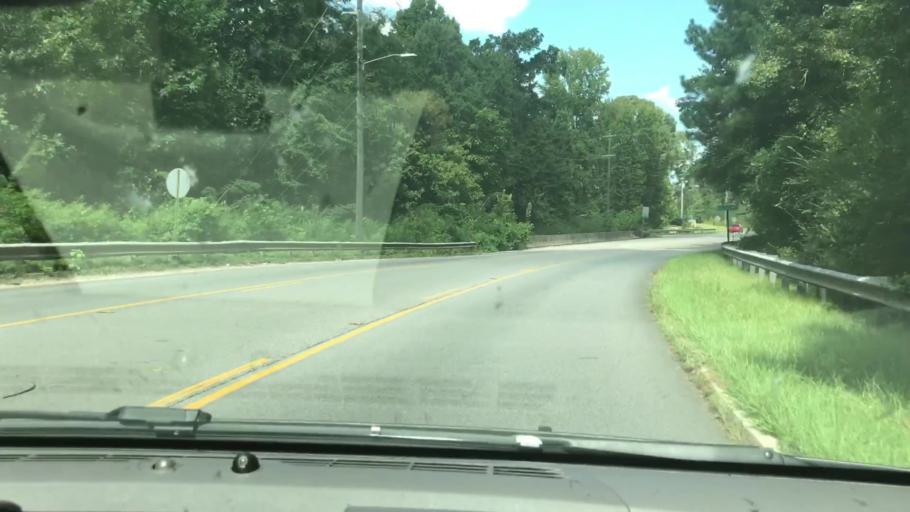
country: US
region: Georgia
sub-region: Troup County
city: La Grange
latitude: 32.9985
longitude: -85.0514
